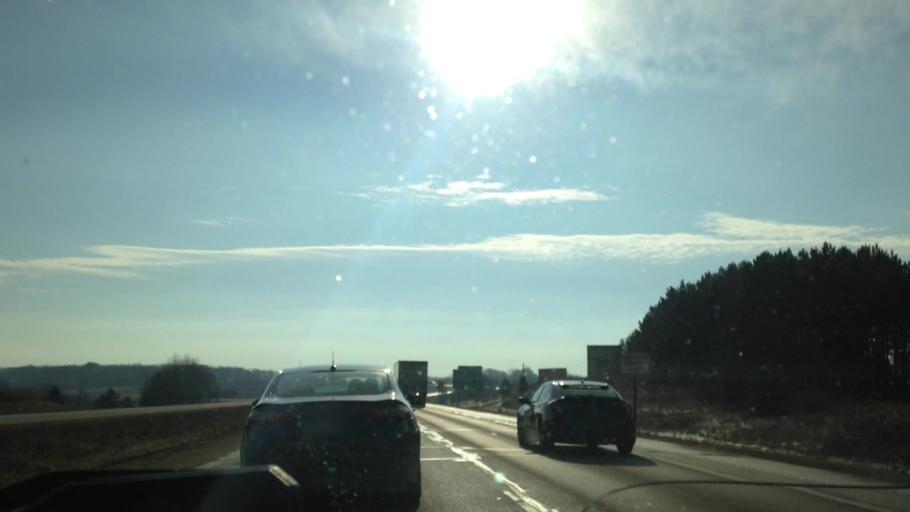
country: US
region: Wisconsin
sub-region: Washington County
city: Slinger
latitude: 43.3287
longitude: -88.2567
